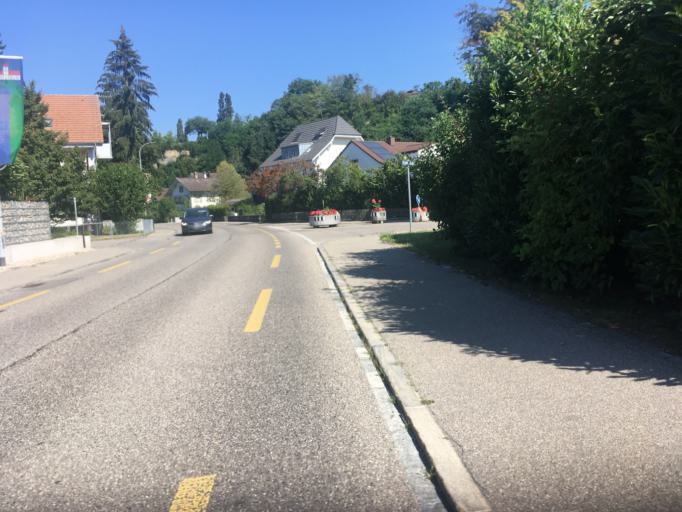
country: CH
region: Bern
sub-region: Emmental District
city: Kirchberg
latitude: 47.0812
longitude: 7.5890
